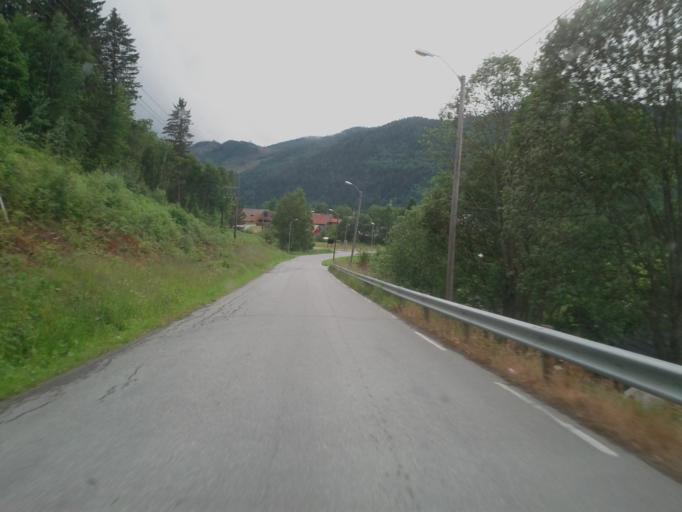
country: NO
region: Sor-Trondelag
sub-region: Melhus
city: Lundamo
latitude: 63.1517
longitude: 10.2968
